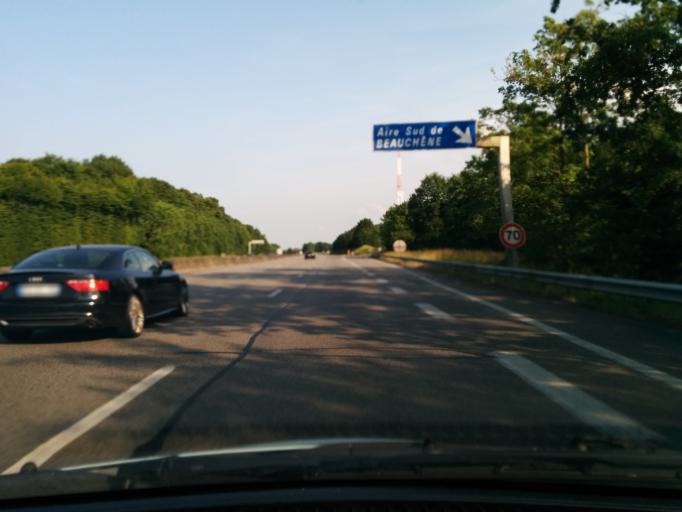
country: FR
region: Haute-Normandie
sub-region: Departement de l'Eure
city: La Chapelle-Reanville
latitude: 49.1074
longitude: 1.3420
